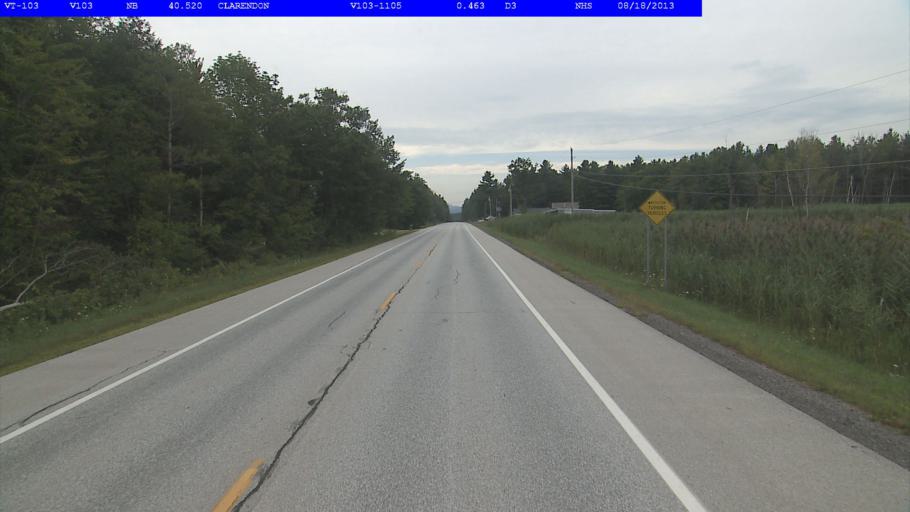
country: US
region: Vermont
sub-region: Rutland County
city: Rutland
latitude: 43.5293
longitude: -72.9360
